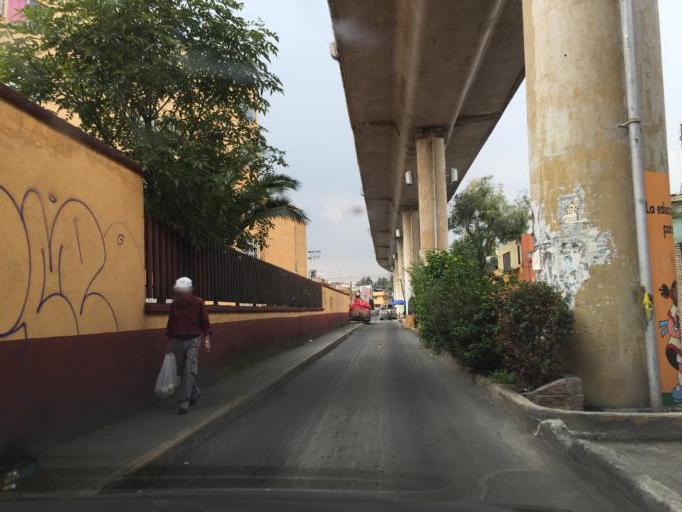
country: MX
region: Mexico City
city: Alvaro Obregon
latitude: 19.3786
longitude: -99.1929
